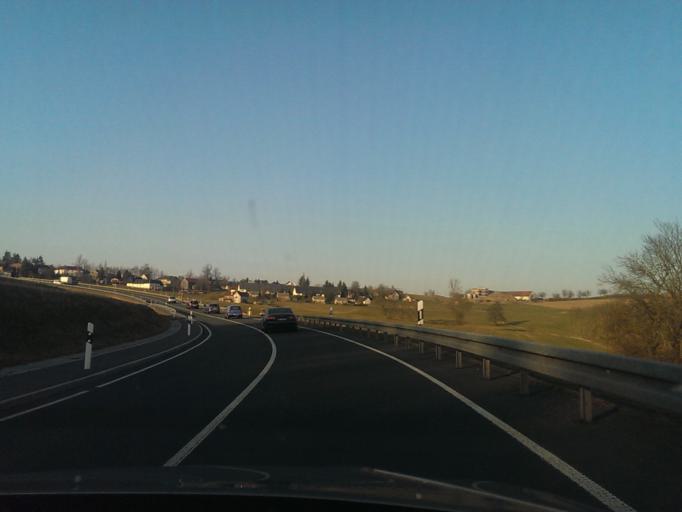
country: DE
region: Saxony
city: Weischlitz
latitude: 50.3986
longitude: 12.0360
